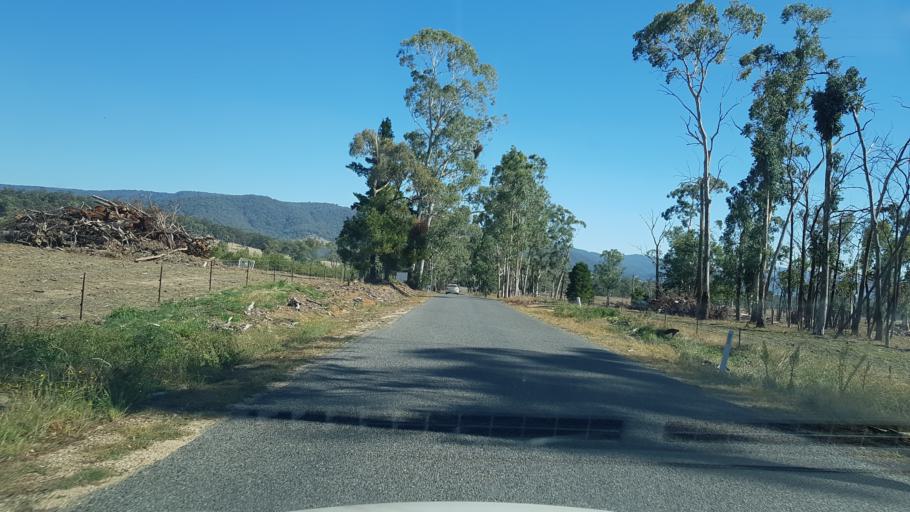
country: AU
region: Victoria
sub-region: Mansfield
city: Mansfield
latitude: -36.8124
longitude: 146.4455
